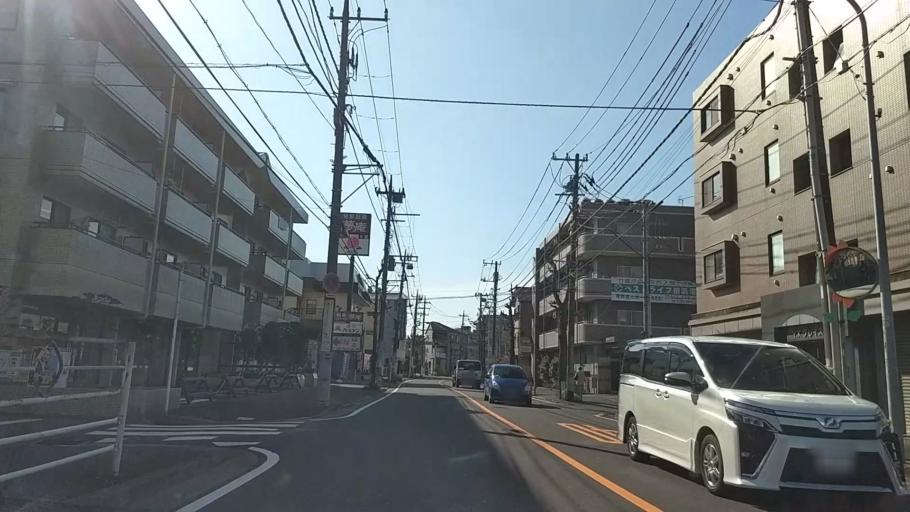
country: JP
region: Kanagawa
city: Yokohama
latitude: 35.3901
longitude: 139.6013
